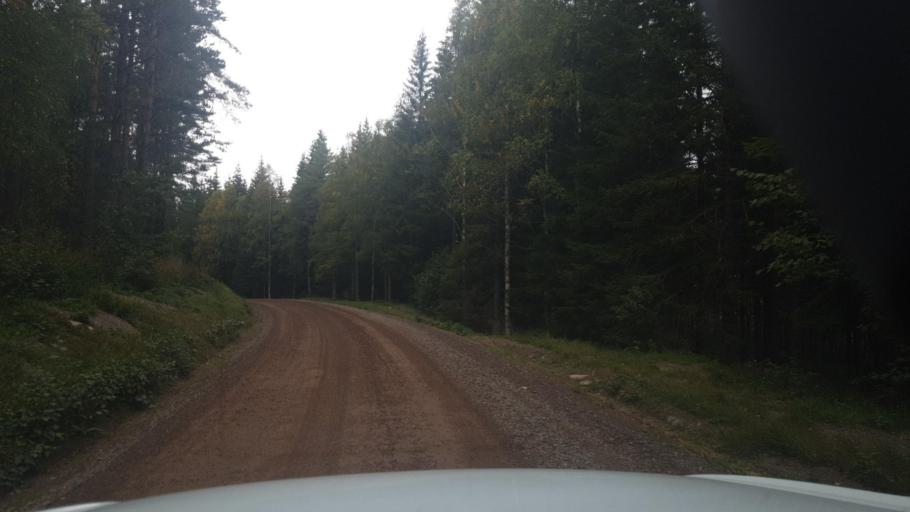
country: SE
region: Vaermland
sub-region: Arvika Kommun
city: Arvika
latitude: 59.9938
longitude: 12.6625
